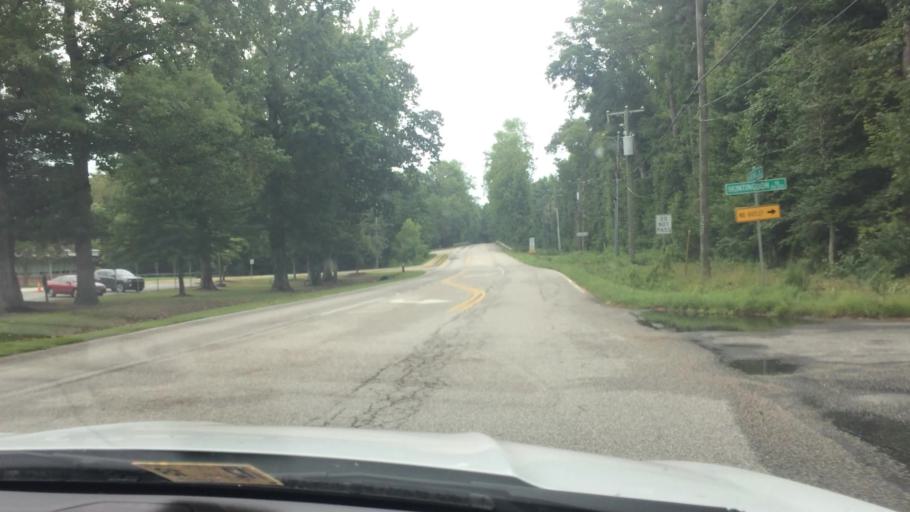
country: US
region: Virginia
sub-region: City of Williamsburg
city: Williamsburg
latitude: 37.2827
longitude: -76.6713
